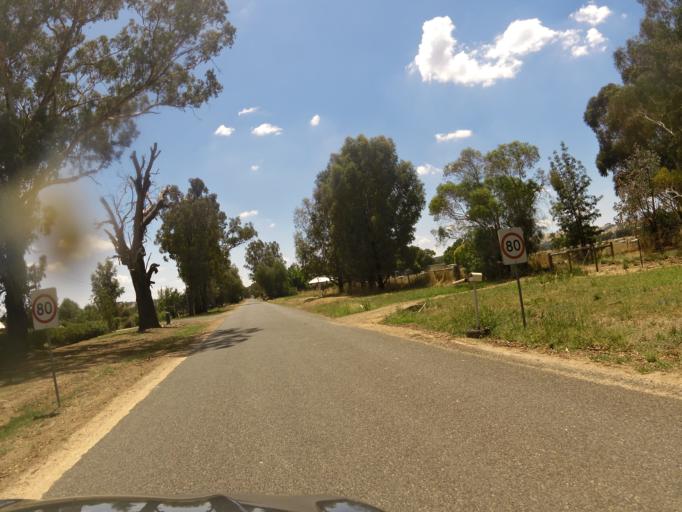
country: AU
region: Victoria
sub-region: Wangaratta
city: Wangaratta
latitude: -36.4313
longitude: 146.5432
